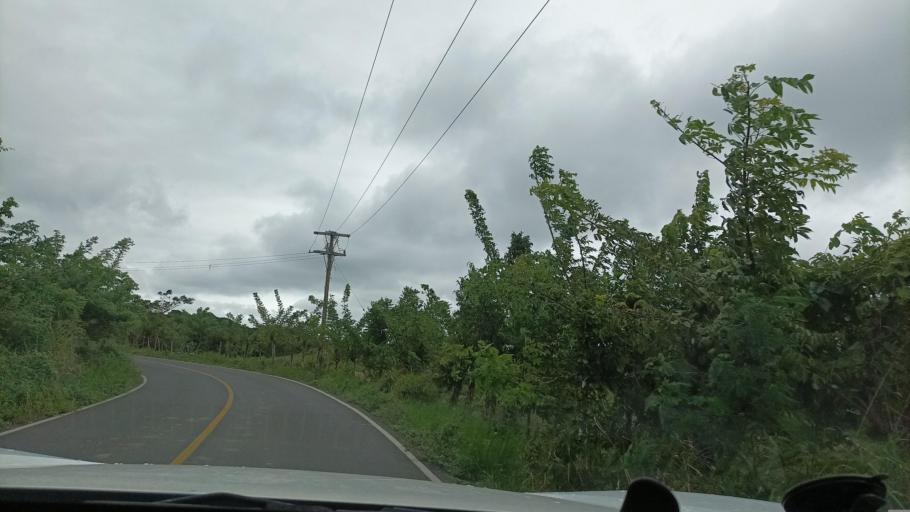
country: MX
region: Veracruz
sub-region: Moloacan
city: Cuichapa
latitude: 17.7899
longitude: -94.3556
